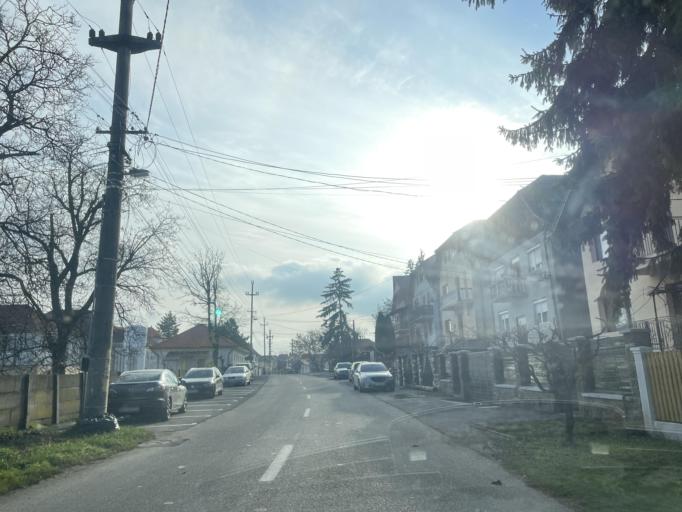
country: RO
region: Mures
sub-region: Municipiul Reghin
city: Reghin
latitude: 46.7835
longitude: 24.6948
